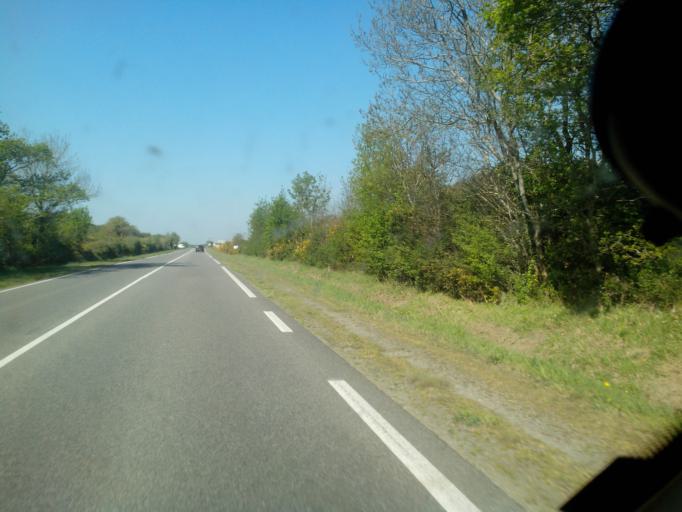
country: FR
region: Pays de la Loire
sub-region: Departement de la Loire-Atlantique
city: La Bernerie-en-Retz
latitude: 47.1123
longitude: -2.0416
